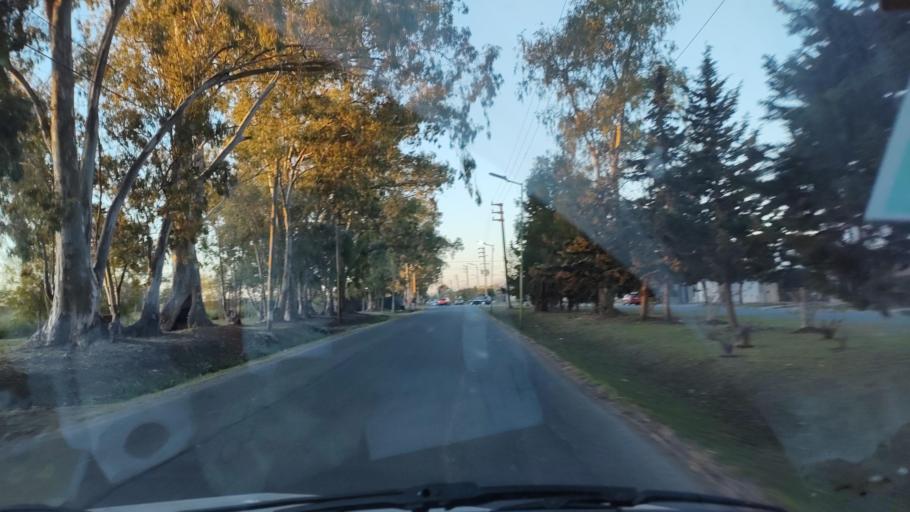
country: AR
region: Buenos Aires
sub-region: Partido de La Plata
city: La Plata
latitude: -34.9032
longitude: -58.0306
